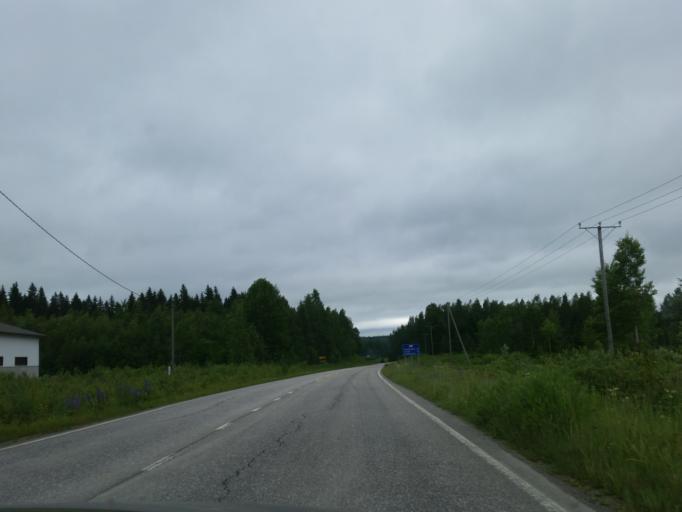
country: FI
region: Northern Savo
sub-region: Koillis-Savo
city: Kaavi
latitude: 62.9730
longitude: 28.5036
